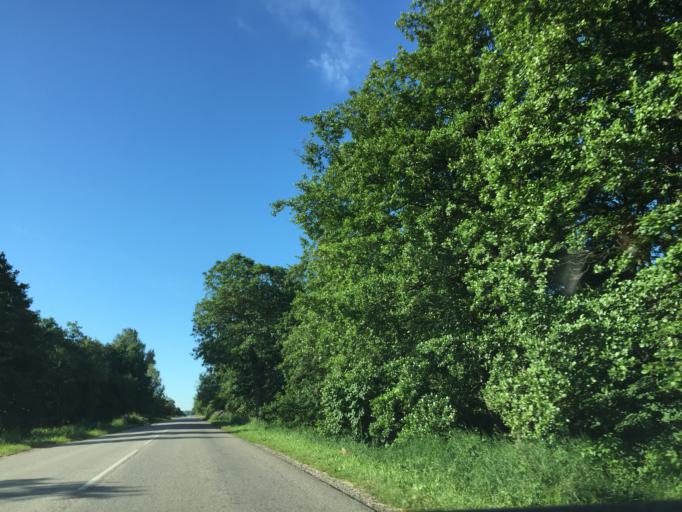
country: LV
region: Ventspils
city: Ventspils
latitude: 57.3552
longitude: 21.6228
